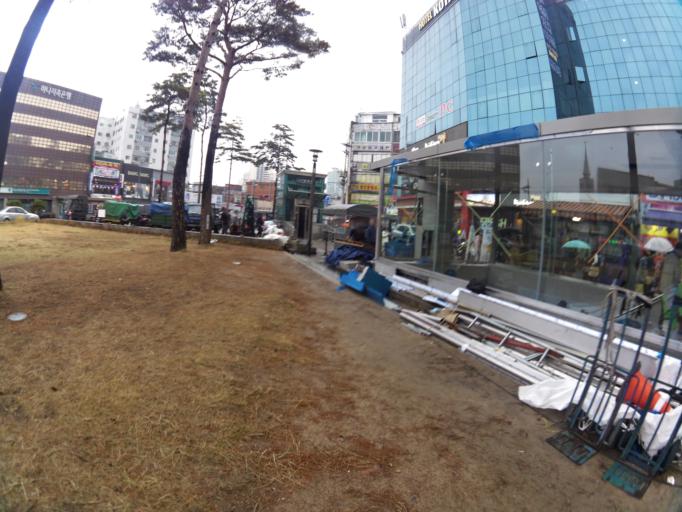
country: KR
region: Seoul
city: Seoul
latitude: 37.5714
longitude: 127.0106
